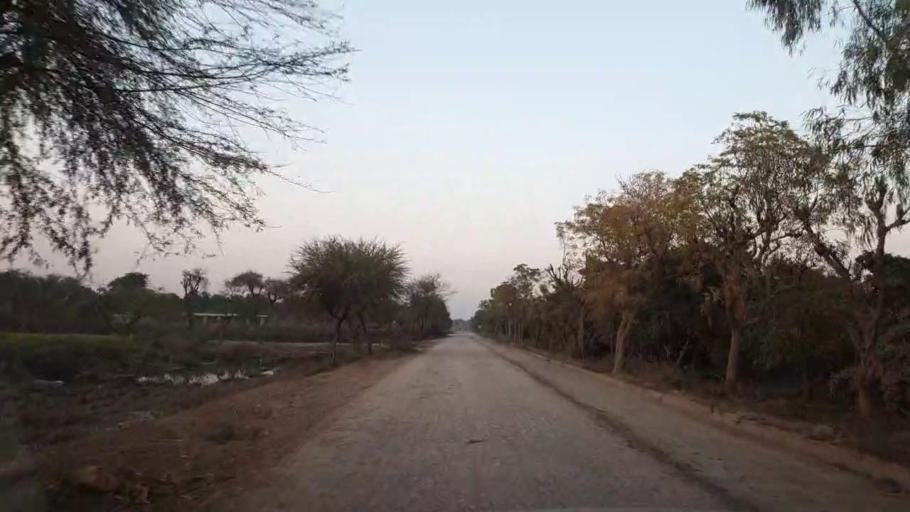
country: PK
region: Sindh
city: Berani
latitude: 25.6618
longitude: 68.7884
